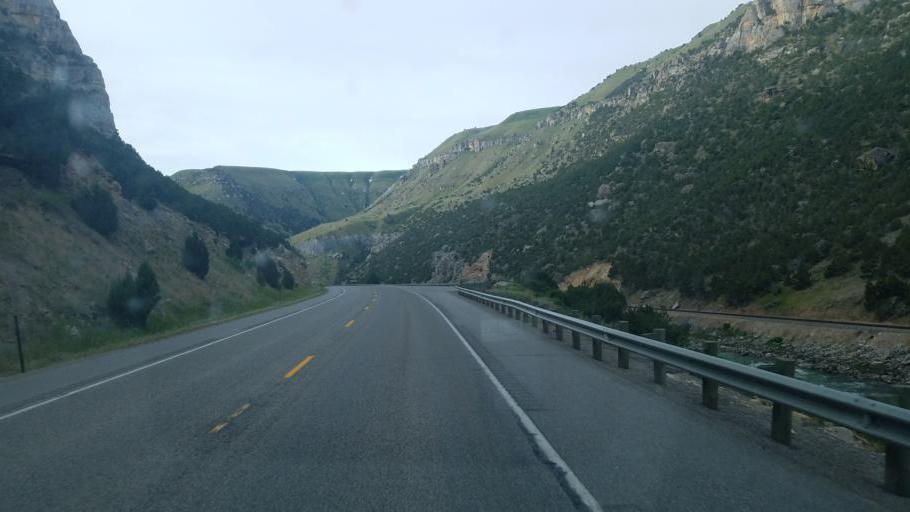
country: US
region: Wyoming
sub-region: Hot Springs County
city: Thermopolis
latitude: 43.5622
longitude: -108.2086
